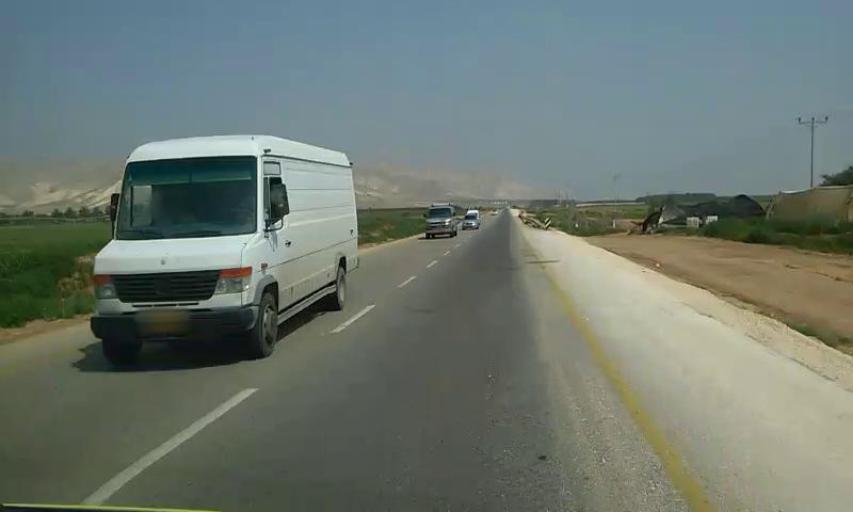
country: PS
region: West Bank
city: Al Fasayil
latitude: 32.0339
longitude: 35.4545
